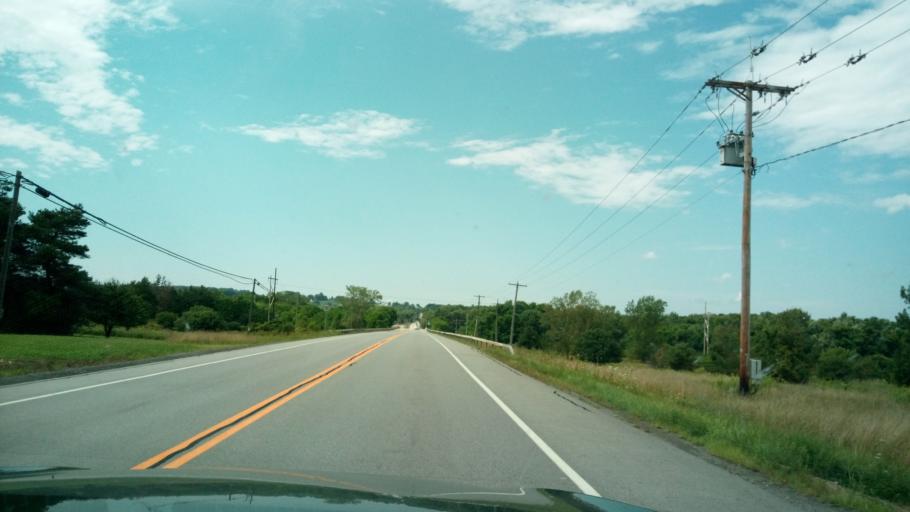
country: US
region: New York
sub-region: Livingston County
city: Geneseo
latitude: 42.8306
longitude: -77.8829
